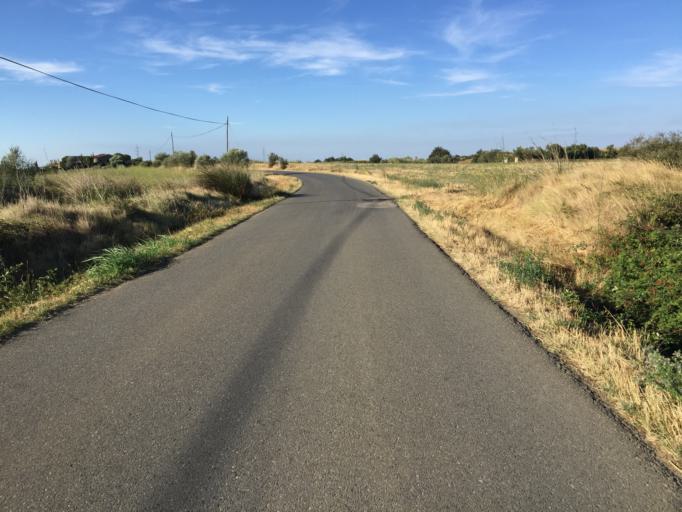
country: ES
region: Catalonia
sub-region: Provincia de Girona
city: Vilajuiga
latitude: 42.2973
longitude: 3.0784
